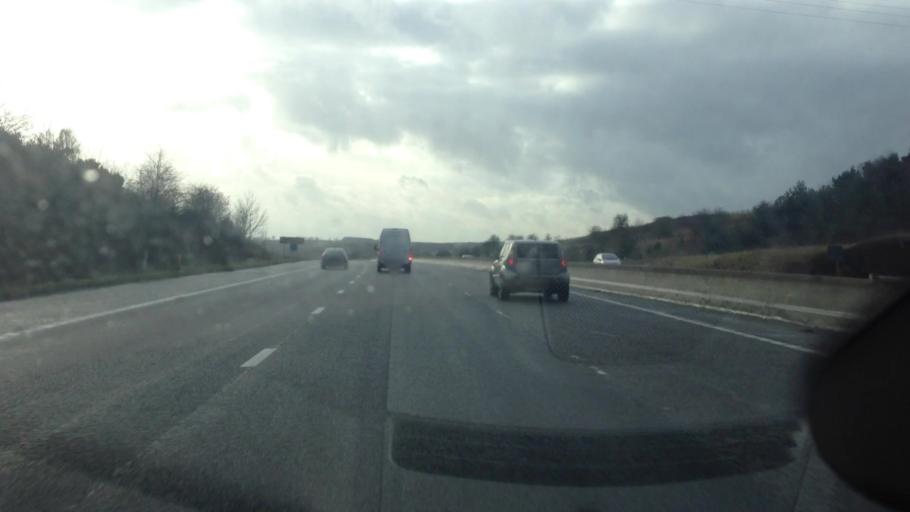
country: GB
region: England
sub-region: City and Borough of Wakefield
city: Crigglestone
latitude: 53.6200
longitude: -1.5494
